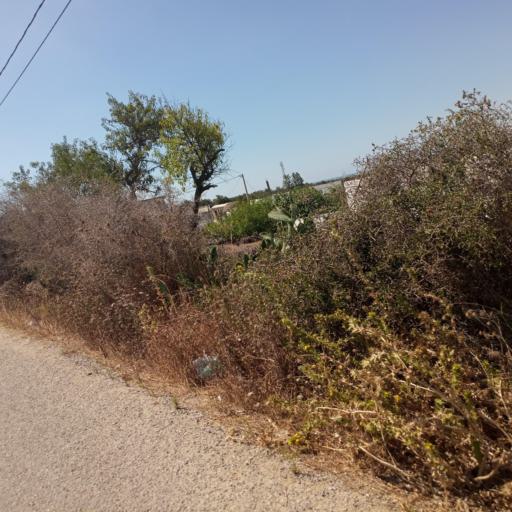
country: TN
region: Nabul
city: Qulaybiyah
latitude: 36.8645
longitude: 11.0343
